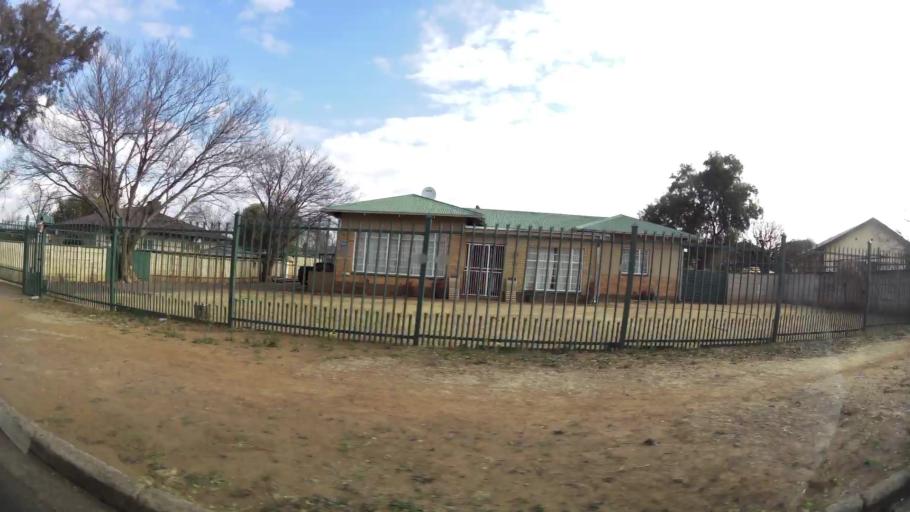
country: ZA
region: Orange Free State
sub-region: Mangaung Metropolitan Municipality
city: Bloemfontein
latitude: -29.0780
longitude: 26.2442
